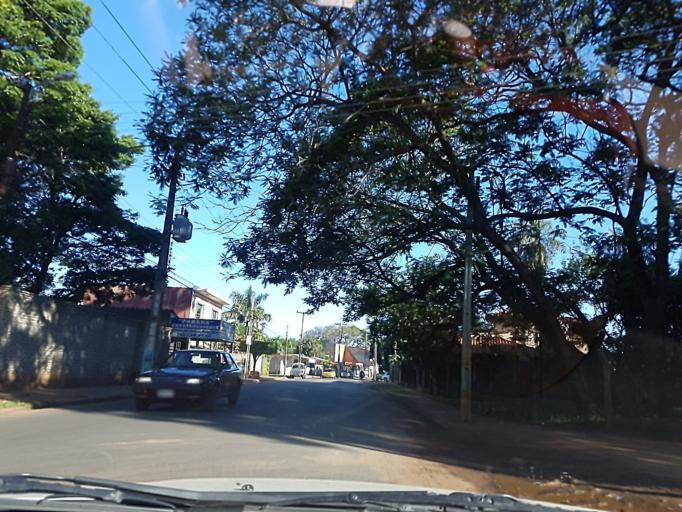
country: PY
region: Central
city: San Lorenzo
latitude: -25.2749
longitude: -57.4741
